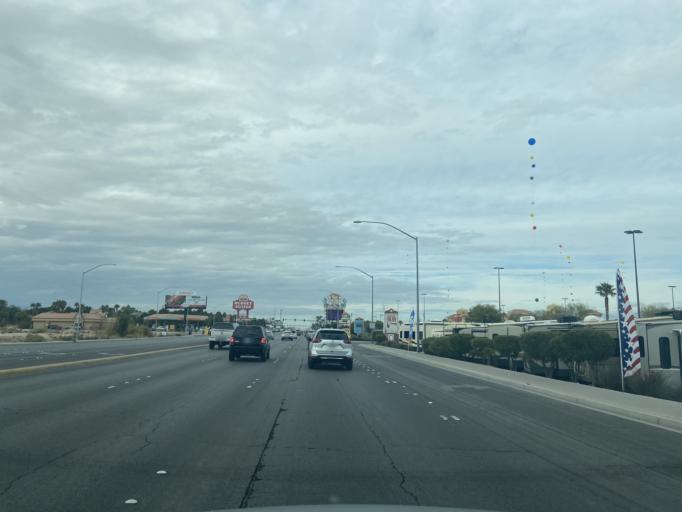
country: US
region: Nevada
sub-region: Clark County
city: Las Vegas
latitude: 36.1985
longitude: -115.1949
